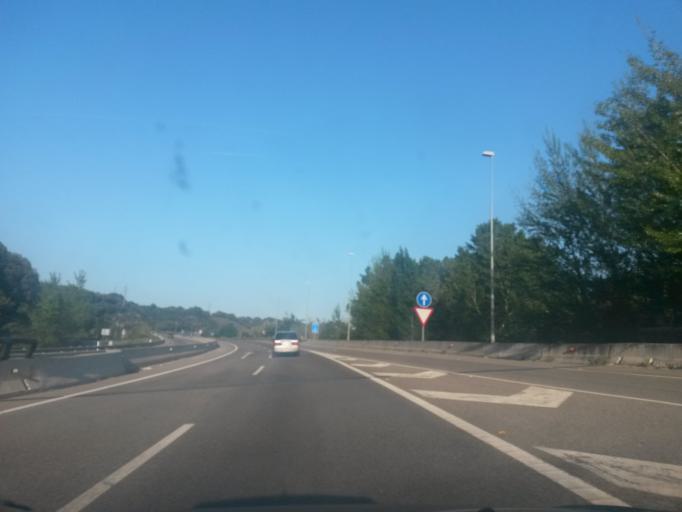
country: ES
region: Catalonia
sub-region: Provincia de Girona
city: Argelaguer
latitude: 42.2153
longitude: 2.6493
